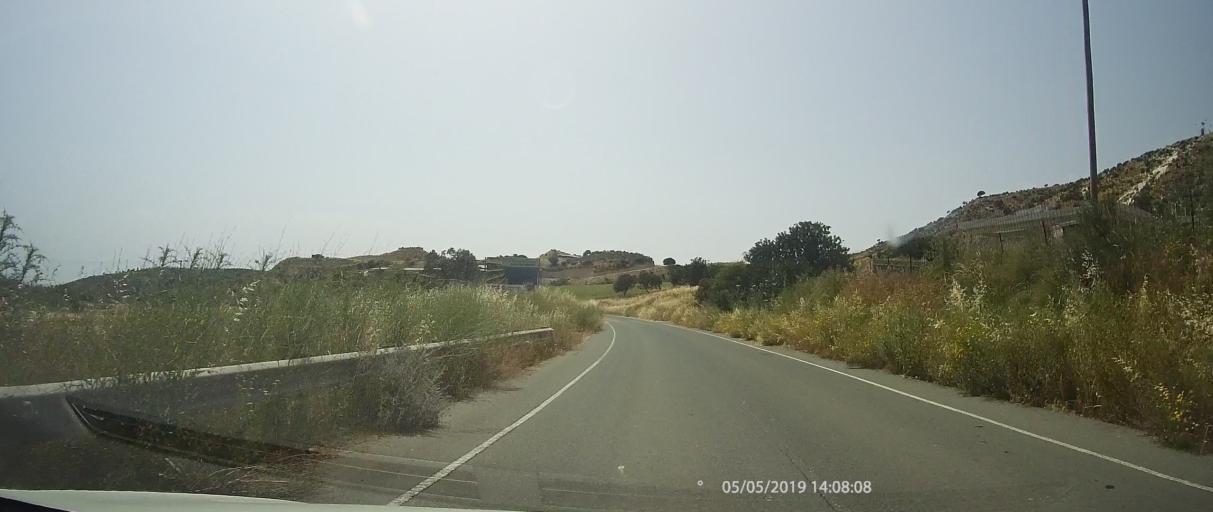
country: CY
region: Limassol
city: Pissouri
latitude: 34.7332
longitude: 32.5880
